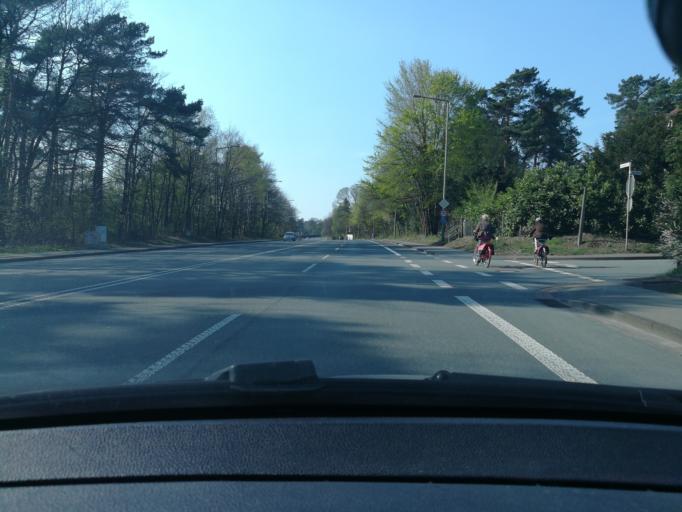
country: DE
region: North Rhine-Westphalia
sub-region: Regierungsbezirk Detmold
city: Bielefeld
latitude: 51.9709
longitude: 8.5492
